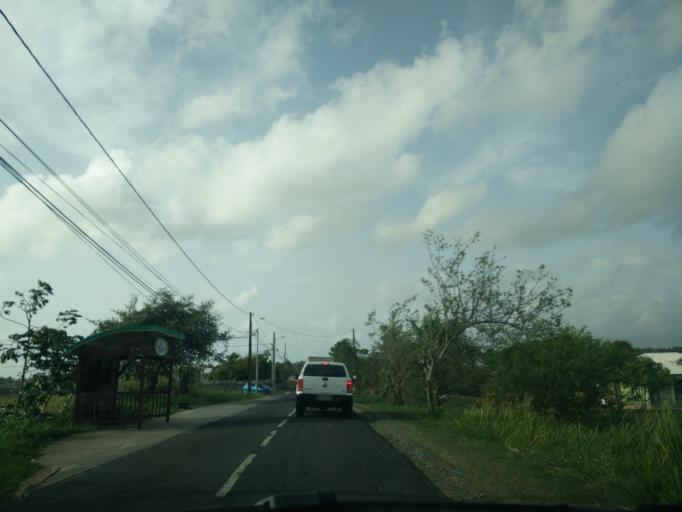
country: GP
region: Guadeloupe
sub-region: Guadeloupe
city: Sainte-Anne
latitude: 16.2736
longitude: -61.3752
